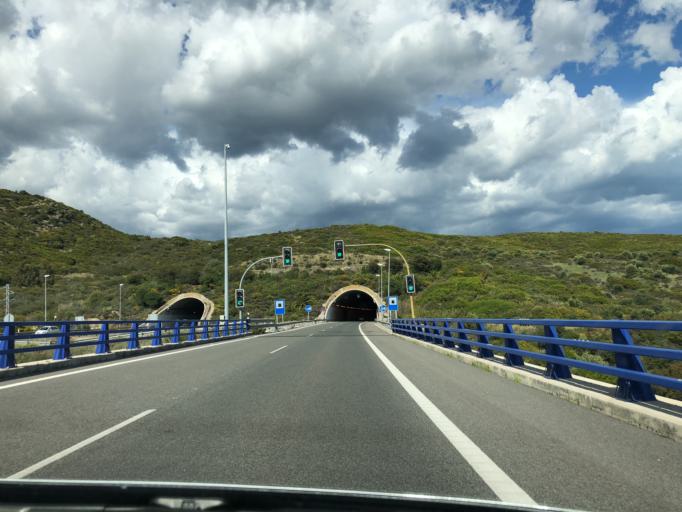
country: ES
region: Andalusia
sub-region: Provincia de Malaga
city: Manilva
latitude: 36.4232
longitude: -5.2145
